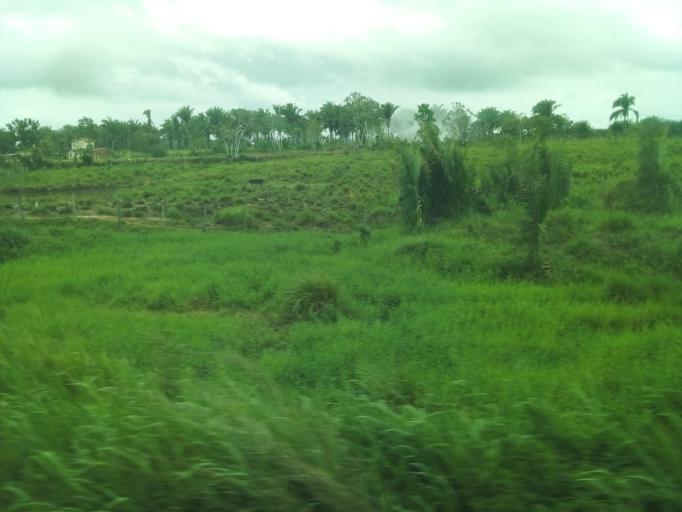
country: BR
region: Maranhao
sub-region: Moncao
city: Moncao
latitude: -3.6283
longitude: -45.1906
